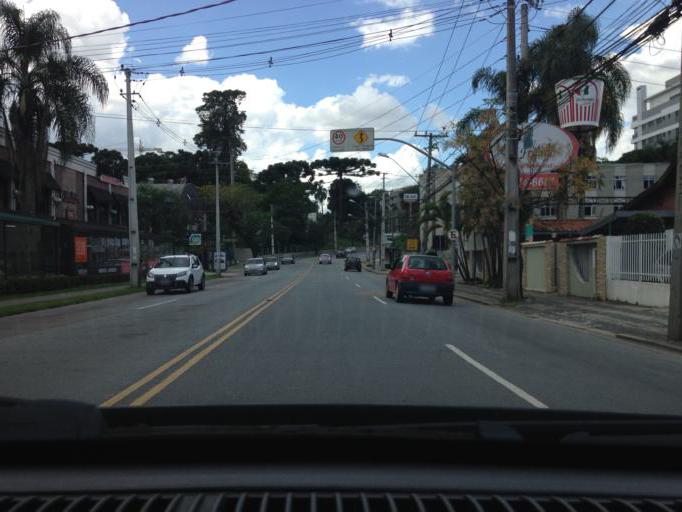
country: BR
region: Parana
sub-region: Curitiba
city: Curitiba
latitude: -25.4079
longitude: -49.2501
